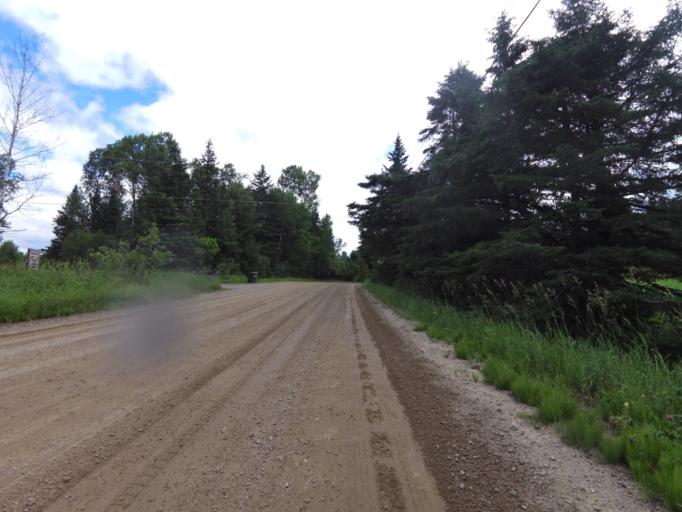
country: CA
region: Quebec
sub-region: Laurentides
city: Mont-Tremblant
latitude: 45.9600
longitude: -74.6342
